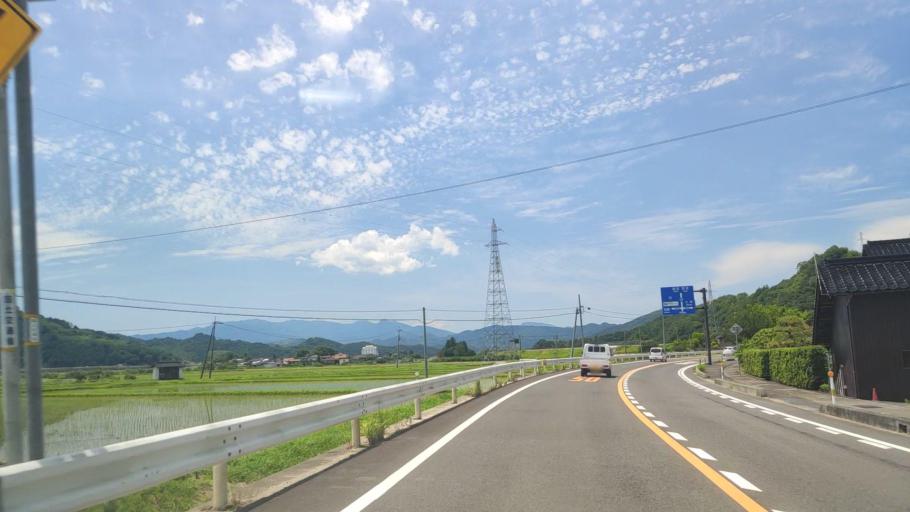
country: JP
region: Tottori
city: Tottori
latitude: 35.3967
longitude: 134.2710
